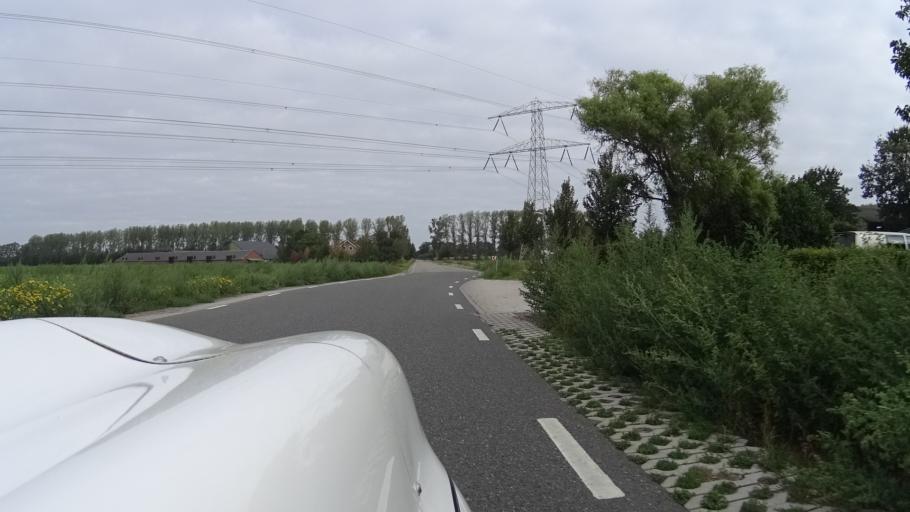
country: NL
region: North Brabant
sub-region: Gemeente Sint Anthonis
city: Sint Anthonis
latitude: 51.6121
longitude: 5.9065
